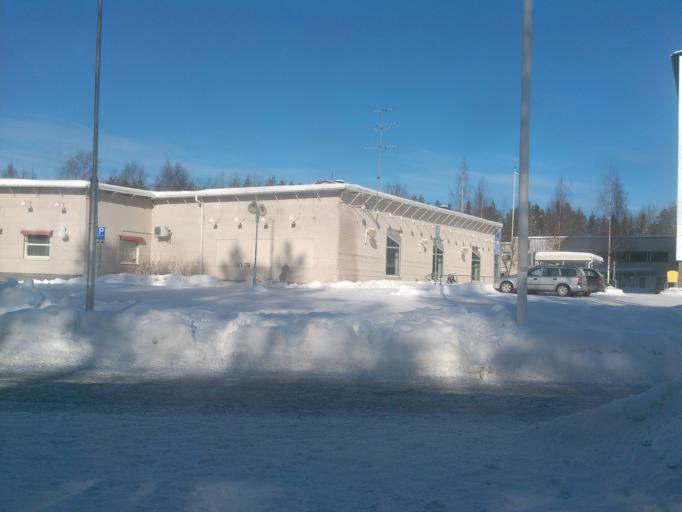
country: SE
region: Vaesterbotten
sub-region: Umea Kommun
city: Ersmark
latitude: 63.8331
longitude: 20.3278
